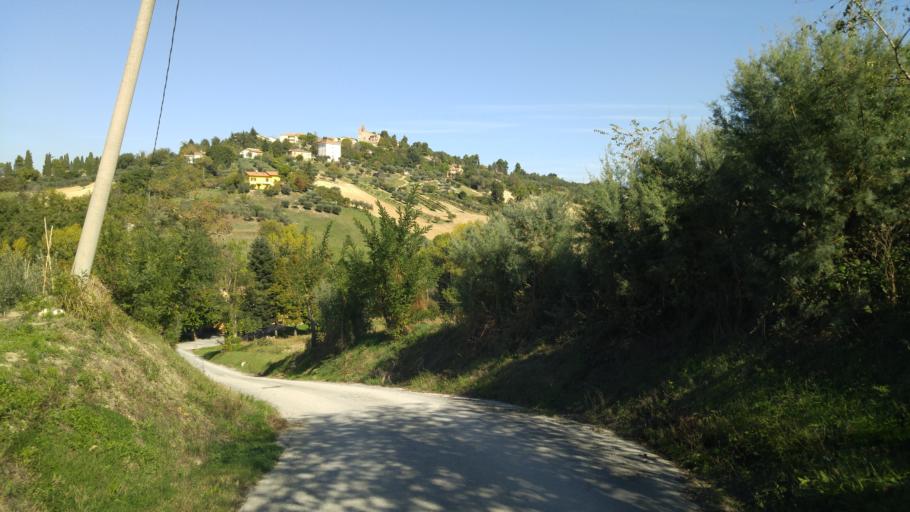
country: IT
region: The Marches
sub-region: Provincia di Pesaro e Urbino
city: Montemaggiore al Metauro
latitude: 43.7315
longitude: 12.9399
